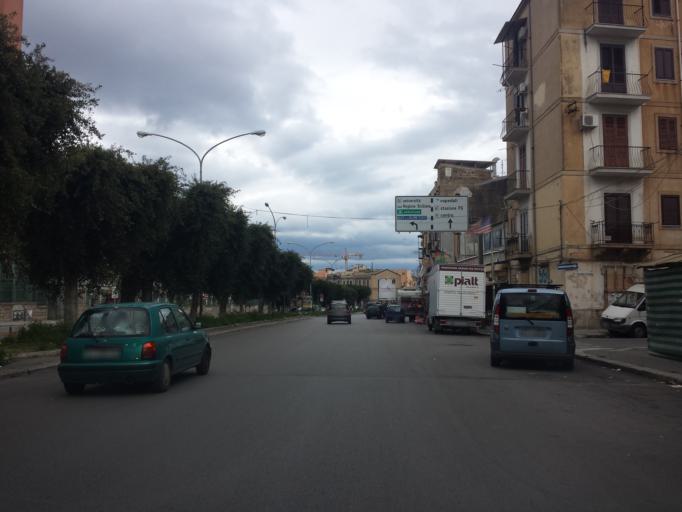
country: IT
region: Sicily
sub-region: Palermo
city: Palermo
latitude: 38.1060
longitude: 13.3523
